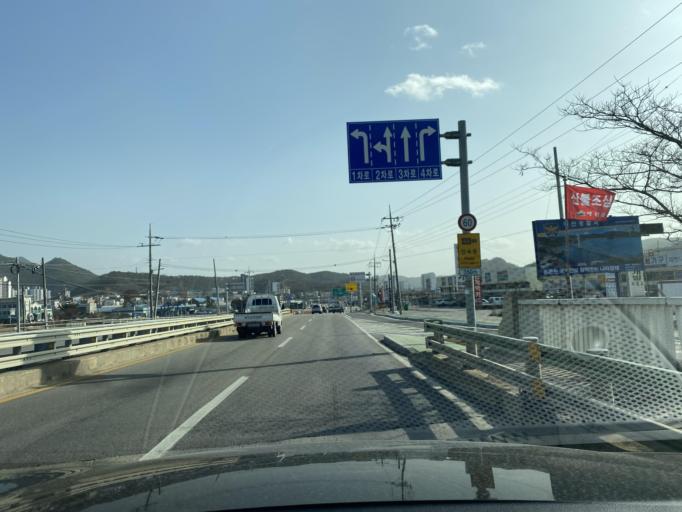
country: KR
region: Chungcheongnam-do
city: Yesan
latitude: 36.6837
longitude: 126.8230
